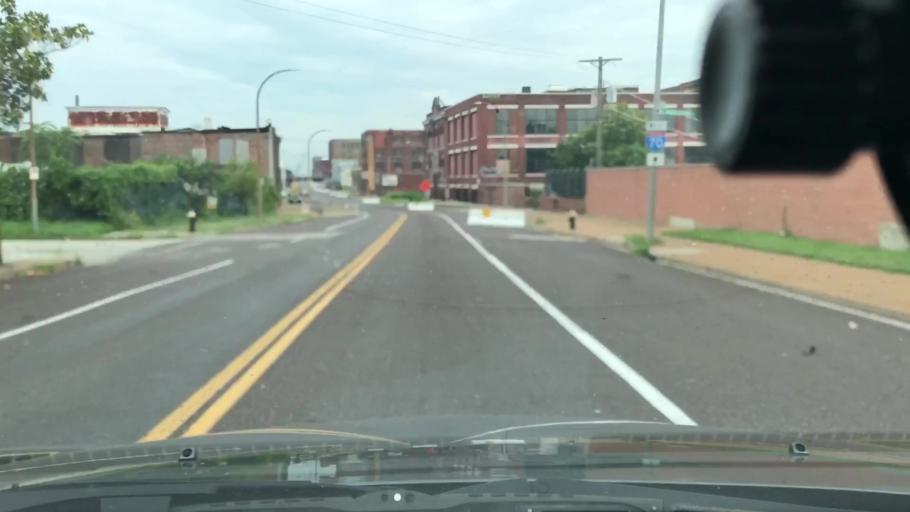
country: US
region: Missouri
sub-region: City of Saint Louis
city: St. Louis
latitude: 38.6451
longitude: -90.1868
